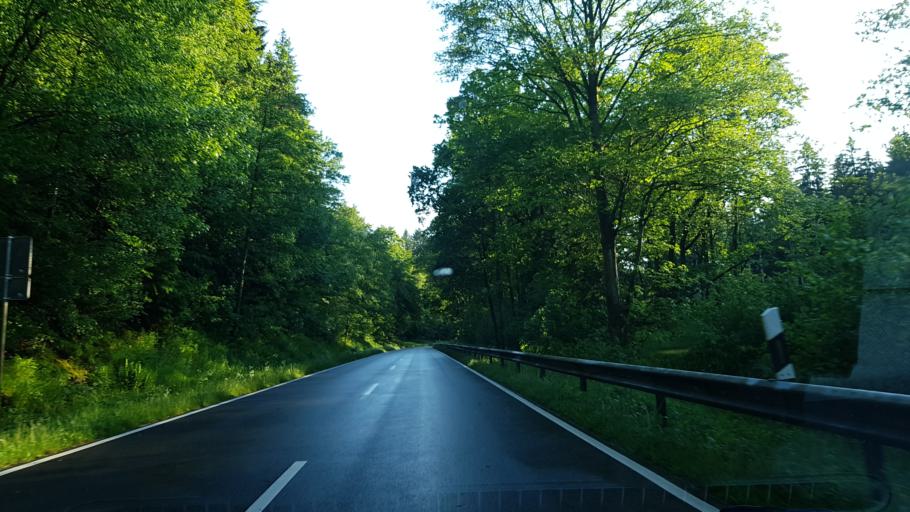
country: DE
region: Lower Saxony
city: Dassel
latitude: 51.7554
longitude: 9.6741
